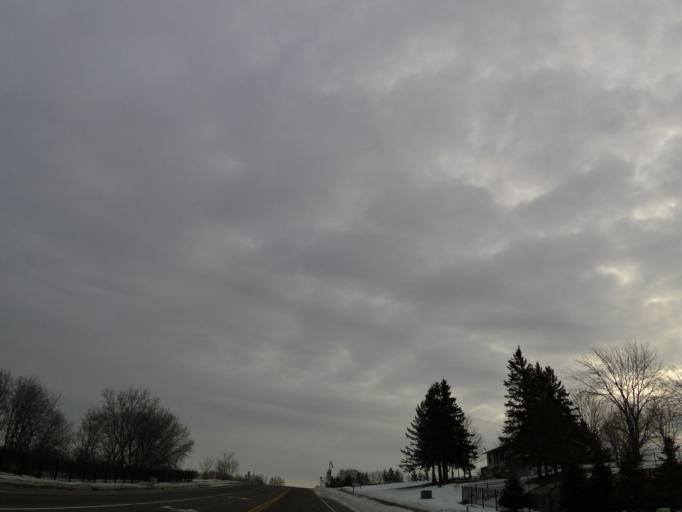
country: US
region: Minnesota
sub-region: Scott County
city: Prior Lake
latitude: 44.7247
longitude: -93.3657
